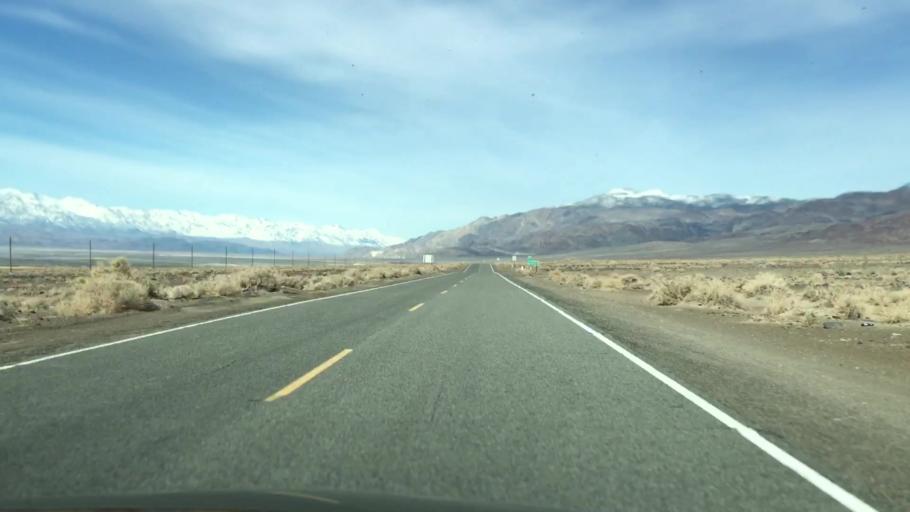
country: US
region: California
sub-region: Inyo County
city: Lone Pine
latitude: 36.4322
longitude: -117.8256
